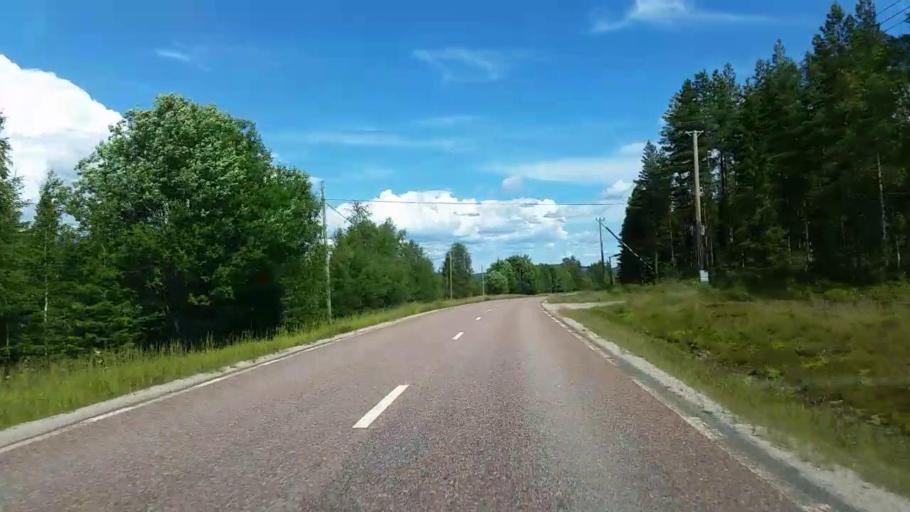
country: SE
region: Dalarna
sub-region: Rattviks Kommun
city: Raettvik
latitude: 61.2051
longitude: 15.3588
